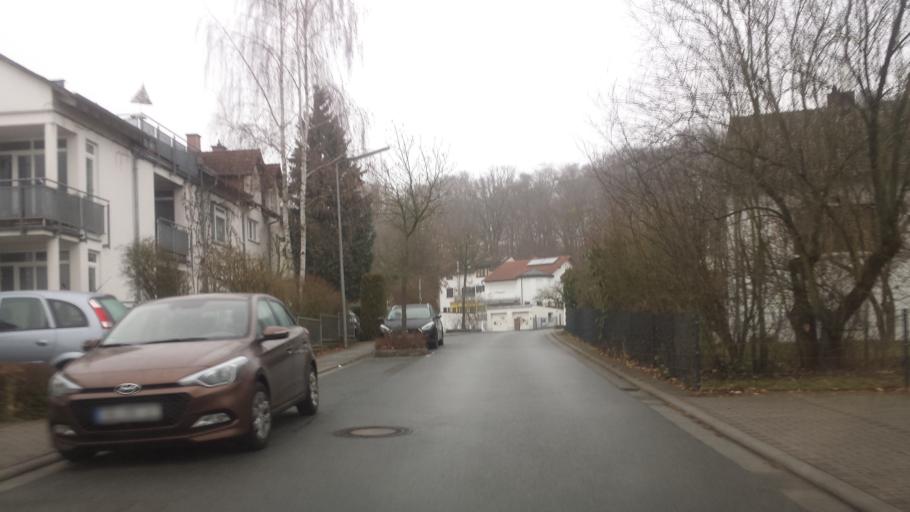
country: DE
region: Hesse
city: Ober-Ramstadt
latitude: 49.8417
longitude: 8.6977
